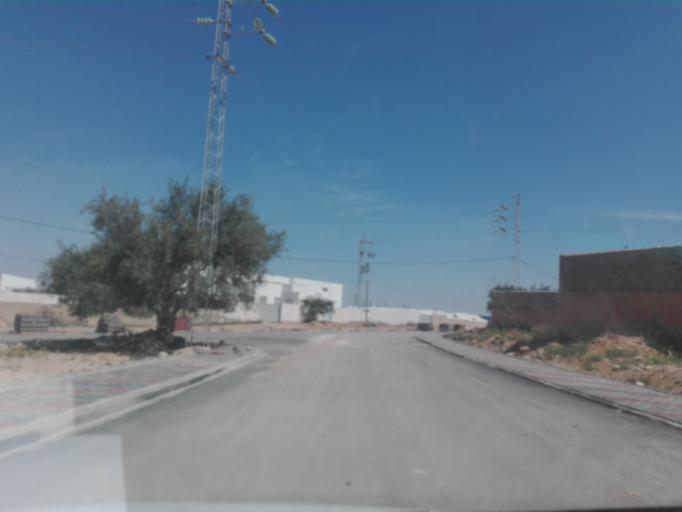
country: TN
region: Safaqis
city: Sfax
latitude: 34.7234
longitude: 10.5151
